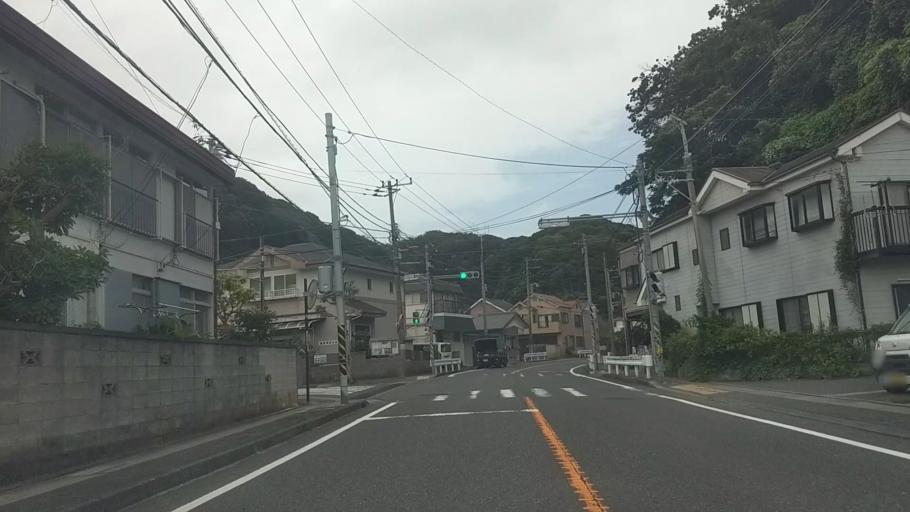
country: JP
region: Kanagawa
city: Yokosuka
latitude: 35.2527
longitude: 139.7371
